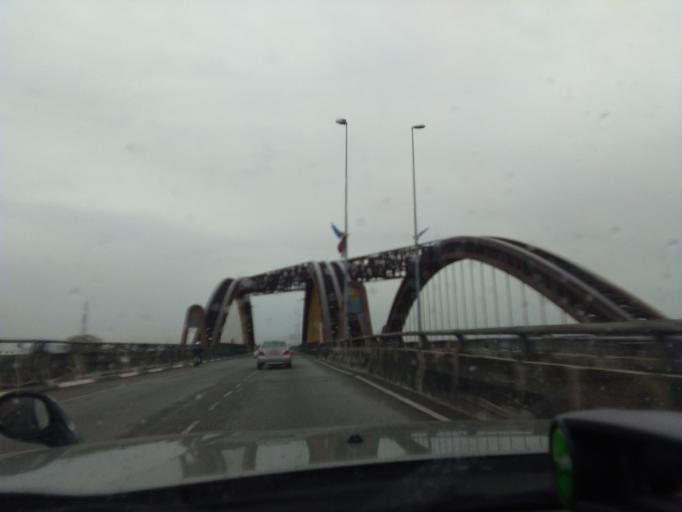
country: MY
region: Penang
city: Nibong Tebal
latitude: 5.1711
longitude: 100.4792
